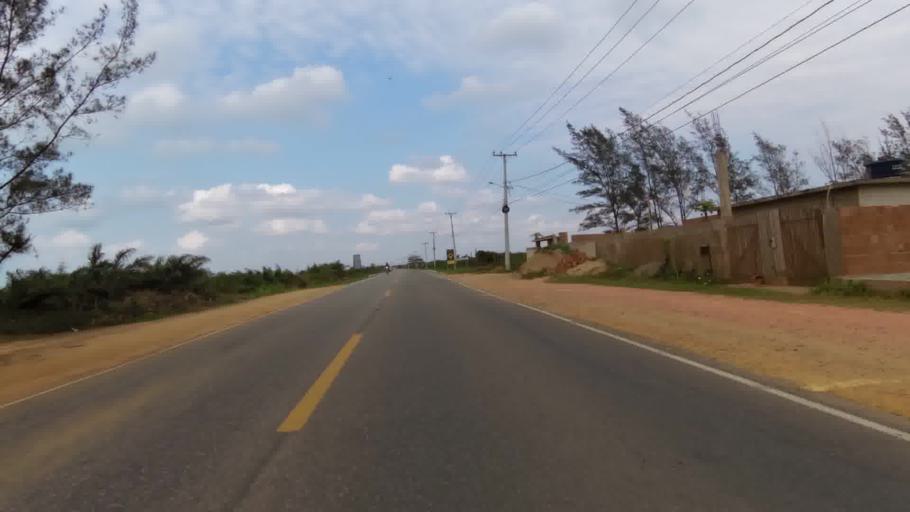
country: BR
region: Espirito Santo
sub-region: Itapemirim
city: Itapemirim
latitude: -20.9180
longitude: -40.7898
